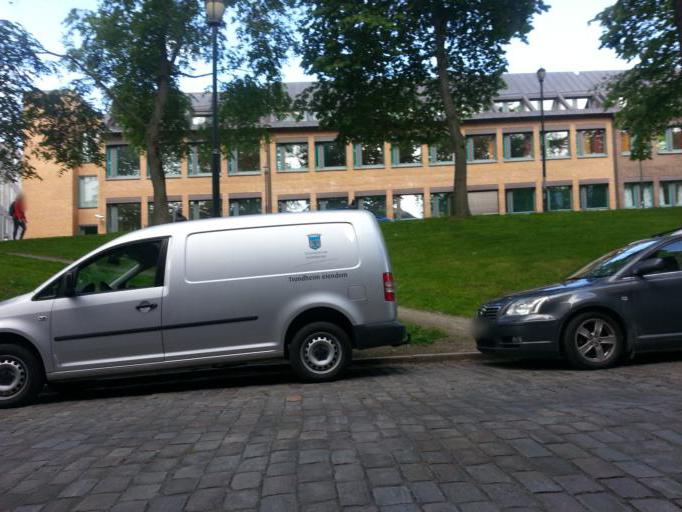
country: NO
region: Sor-Trondelag
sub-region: Trondheim
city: Trondheim
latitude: 63.4310
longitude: 10.4026
